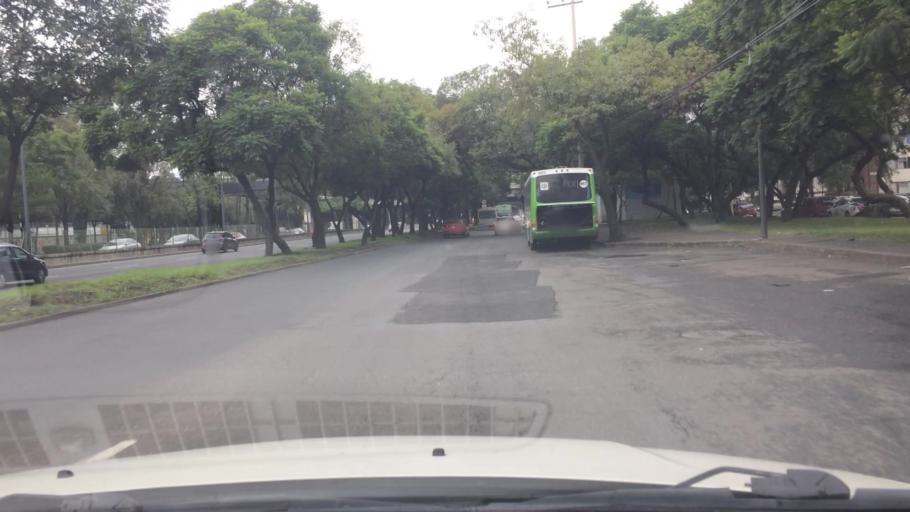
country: MX
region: Mexico City
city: Xochimilco
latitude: 19.2861
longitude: -99.1231
